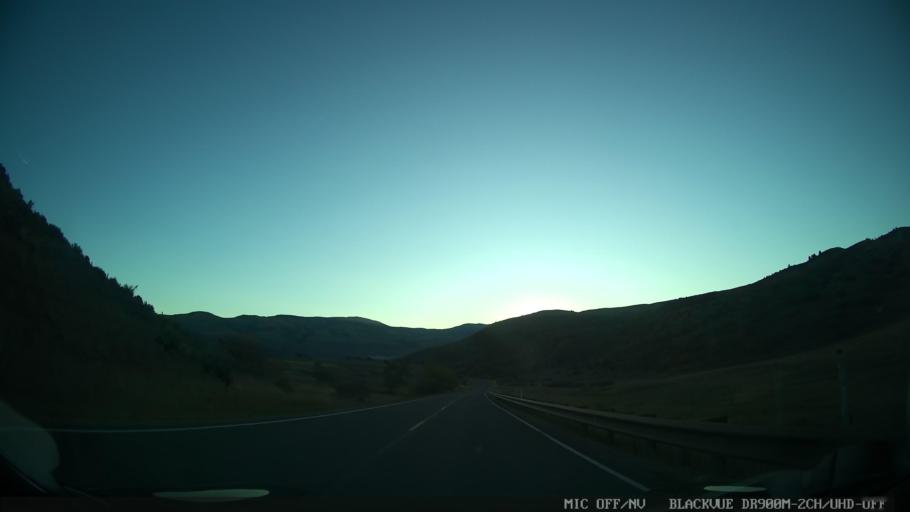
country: US
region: Colorado
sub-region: Eagle County
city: Edwards
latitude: 39.8172
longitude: -106.6580
